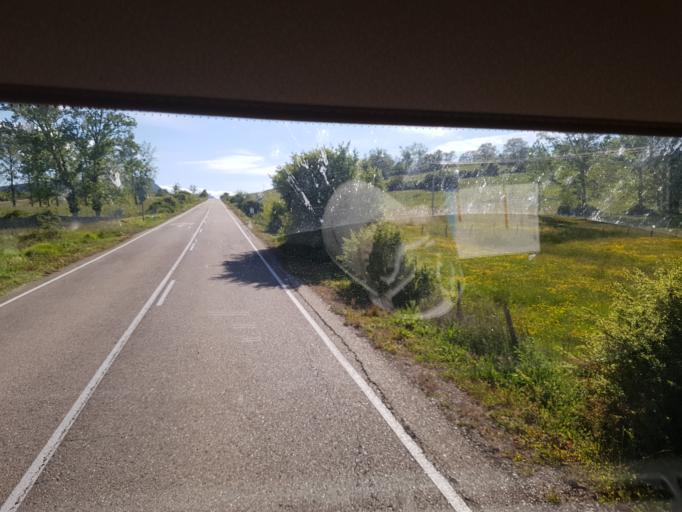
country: ES
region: Castille and Leon
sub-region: Provincia de Burgos
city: Espinosa de los Monteros
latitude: 43.0597
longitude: -3.5976
